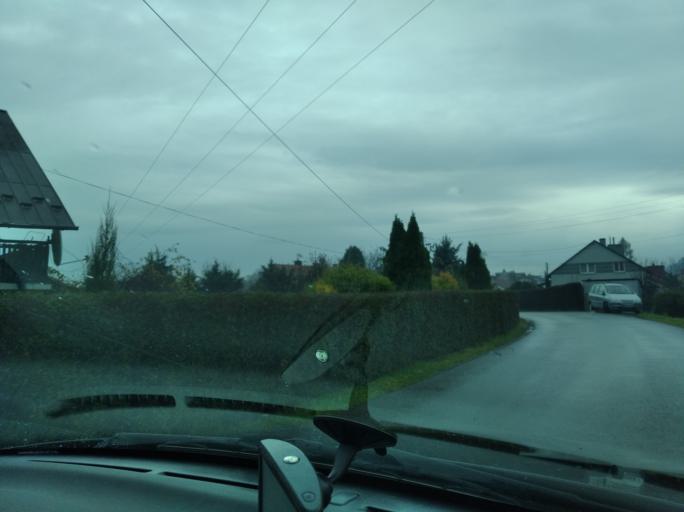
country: PL
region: Subcarpathian Voivodeship
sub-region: Powiat strzyzowski
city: Czudec
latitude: 49.9414
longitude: 21.8418
